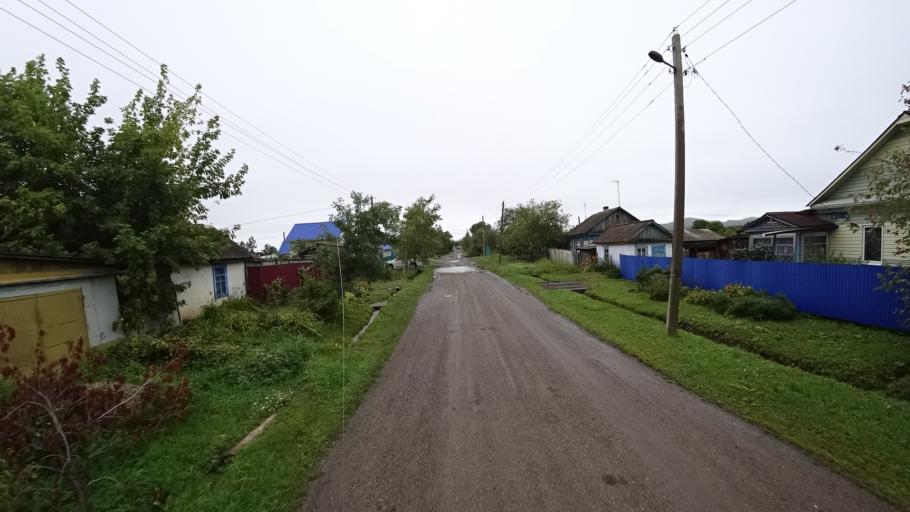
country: RU
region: Primorskiy
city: Monastyrishche
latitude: 44.2083
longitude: 132.4517
